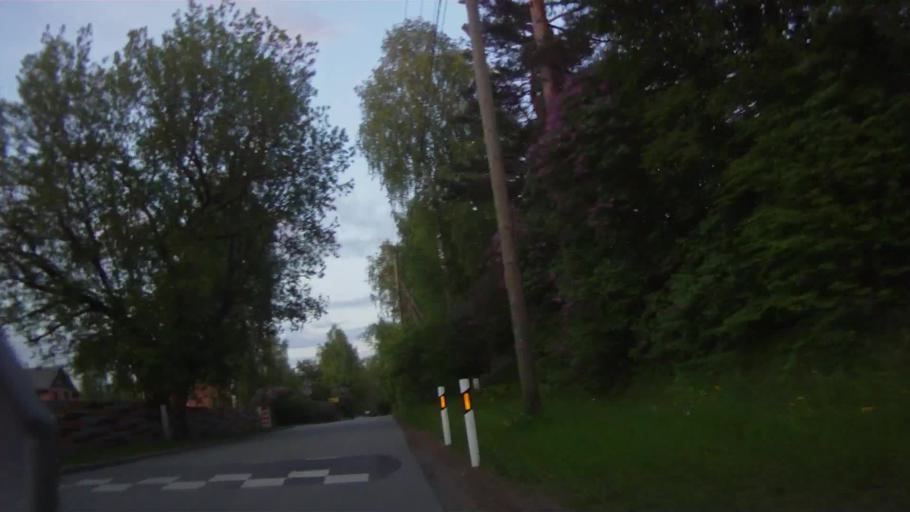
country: LV
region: Riga
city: Bergi
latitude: 56.9979
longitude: 24.2801
